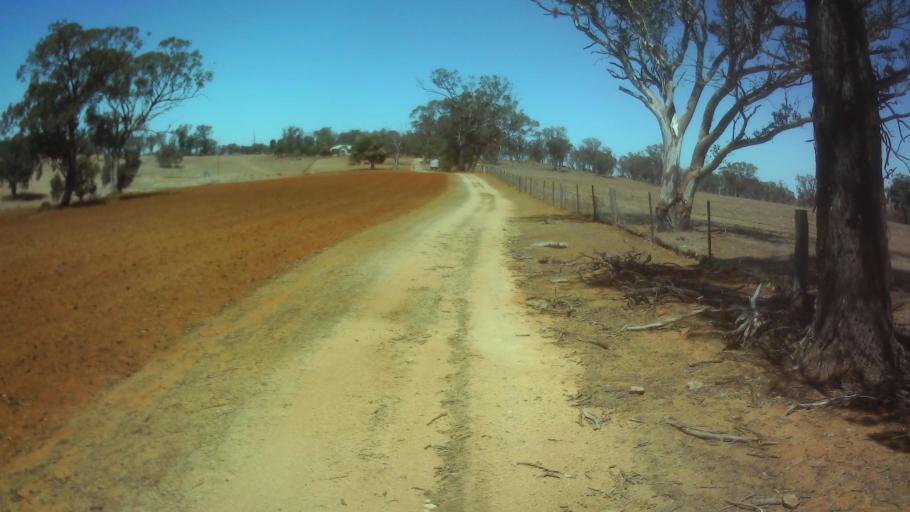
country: AU
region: New South Wales
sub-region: Cowra
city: Cowra
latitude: -33.9067
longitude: 148.5078
